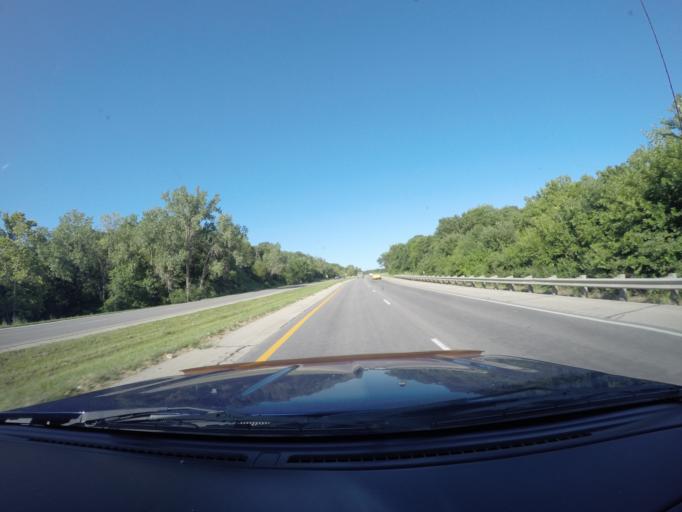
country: US
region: Kansas
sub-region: Shawnee County
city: Topeka
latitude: 39.0926
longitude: -95.6198
